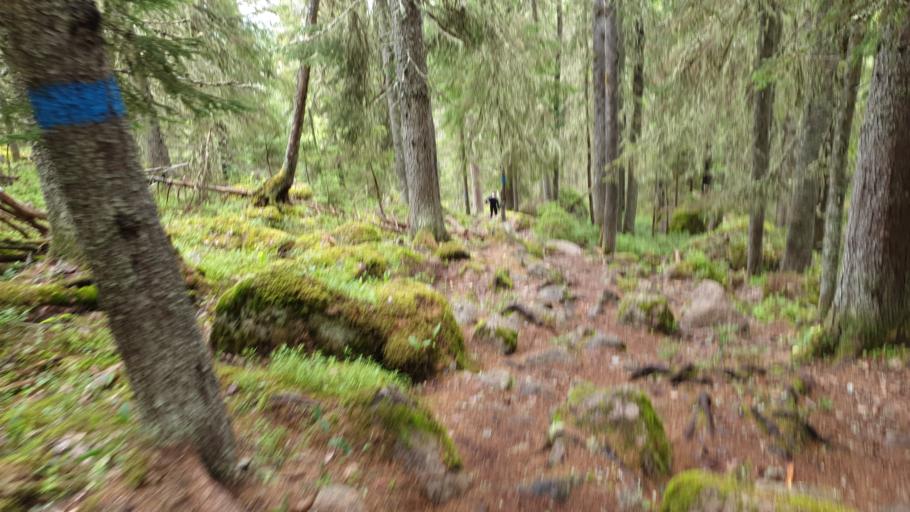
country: SE
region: Gaevleborg
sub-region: Hudiksvalls Kommun
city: Sorforsa
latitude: 61.6413
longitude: 16.7675
